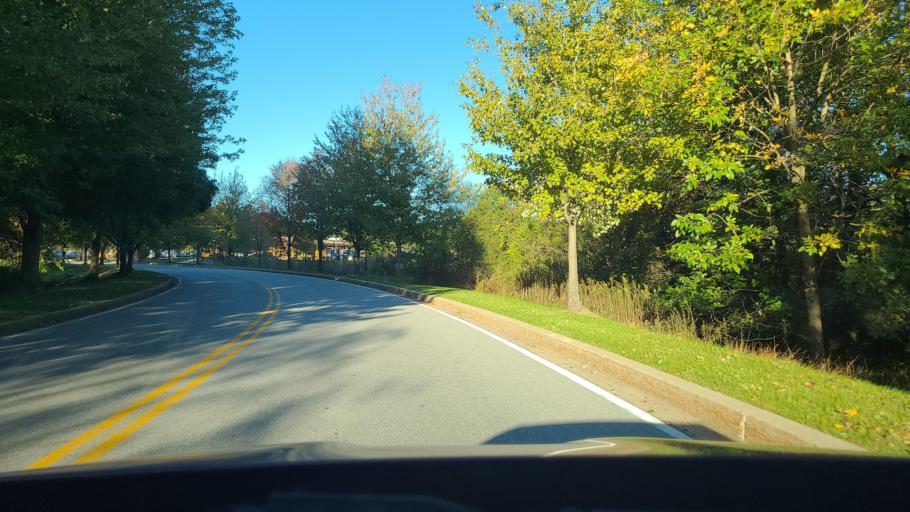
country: US
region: Maryland
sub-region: Carroll County
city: Westminster
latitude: 39.5935
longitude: -77.0006
